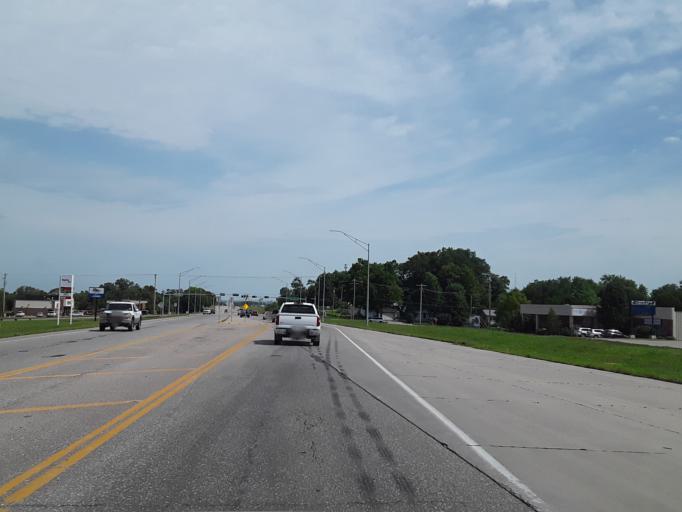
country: US
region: Nebraska
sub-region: Cass County
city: Plattsmouth
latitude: 41.0113
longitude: -95.9086
